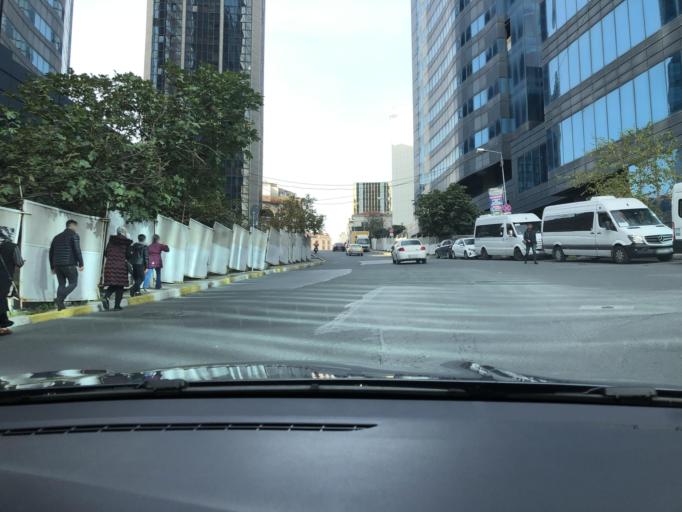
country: TR
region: Istanbul
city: Sisli
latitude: 41.0599
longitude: 28.9909
